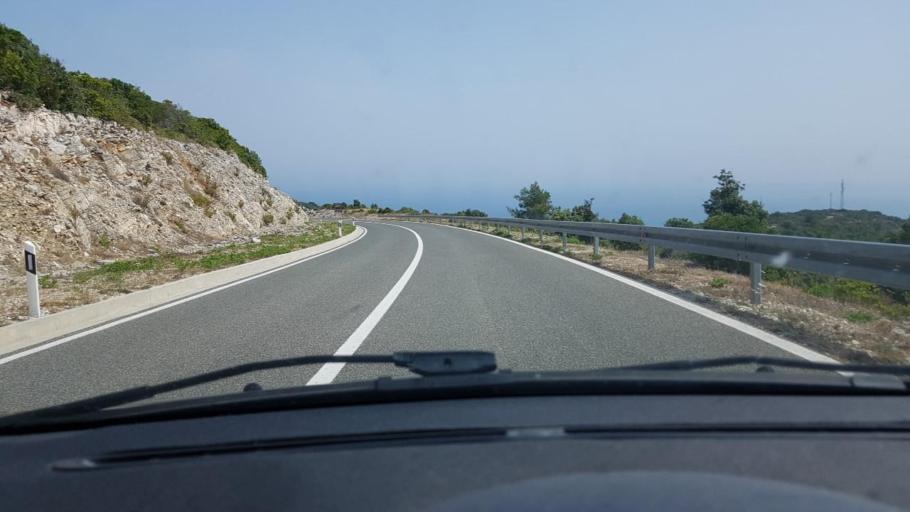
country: HR
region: Dubrovacko-Neretvanska
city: Smokvica
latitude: 42.9453
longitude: 16.9537
